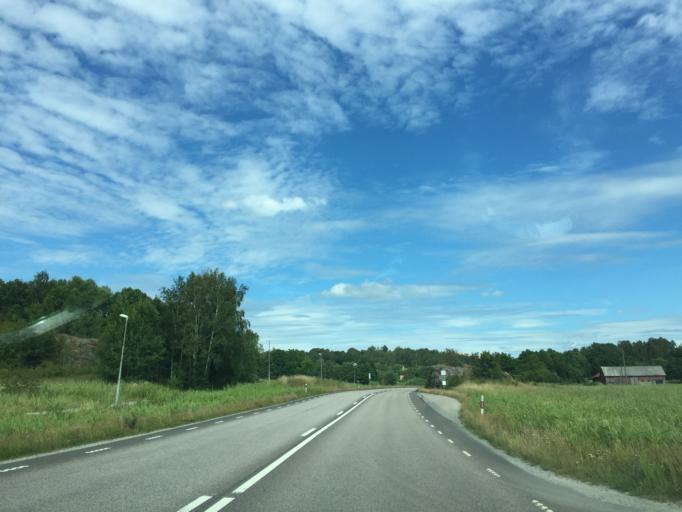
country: SE
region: Vaestra Goetaland
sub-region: Tjorns Kommun
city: Myggenas
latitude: 58.0439
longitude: 11.7436
